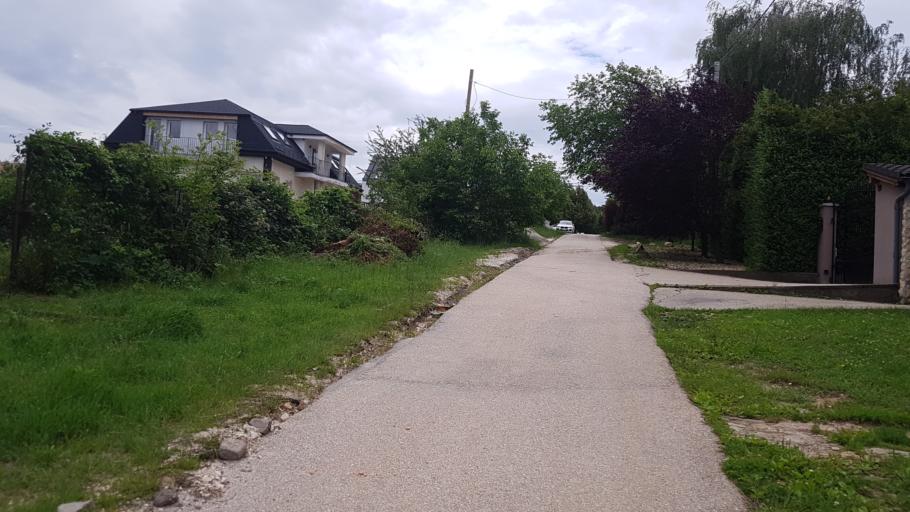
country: HU
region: Pest
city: Urom
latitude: 47.6150
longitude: 19.0172
